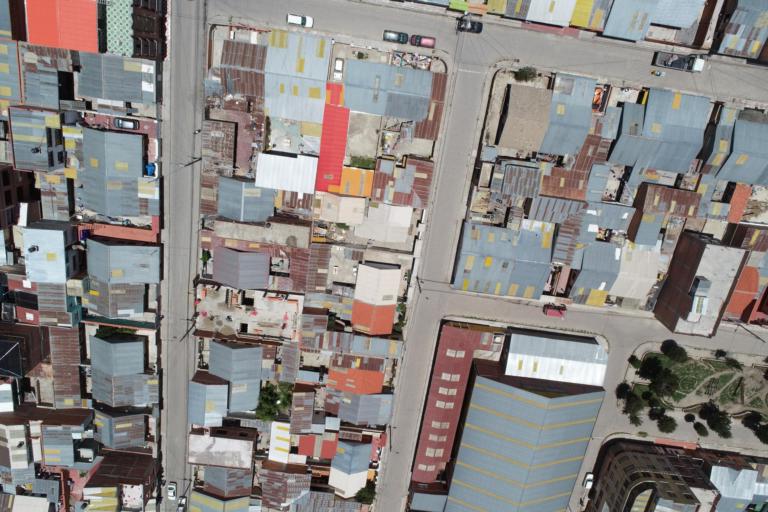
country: BO
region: La Paz
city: La Paz
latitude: -16.5245
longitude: -68.1545
